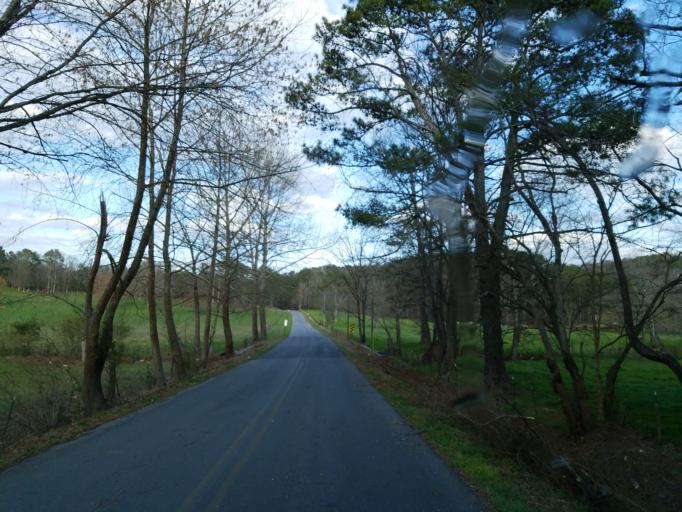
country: US
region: Georgia
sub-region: Bartow County
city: Rydal
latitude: 34.4787
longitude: -84.6754
